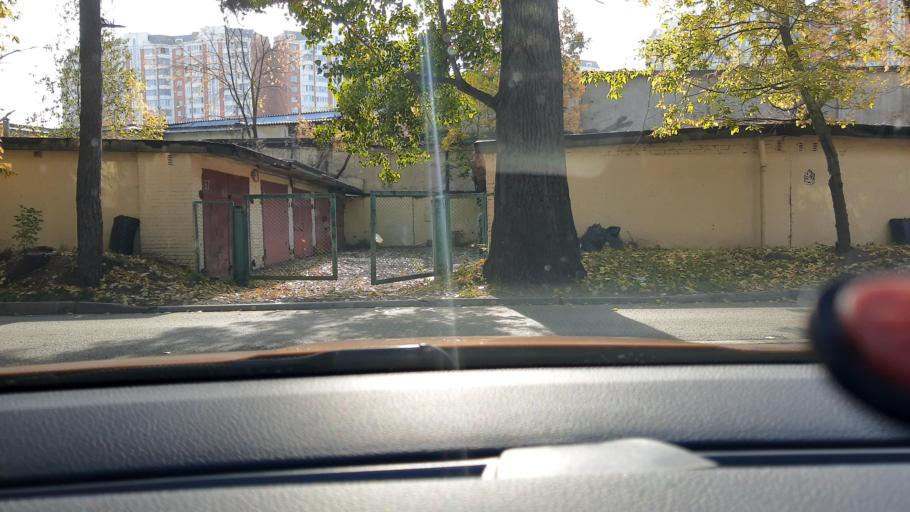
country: RU
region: Moscow
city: Leonovo
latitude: 55.8577
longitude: 37.6433
